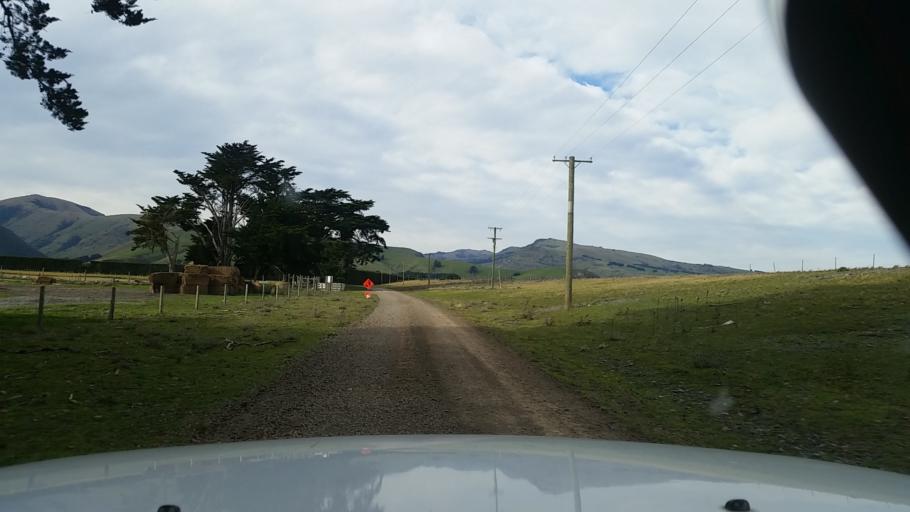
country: NZ
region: Canterbury
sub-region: Selwyn District
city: Lincoln
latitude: -43.8116
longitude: 172.6635
